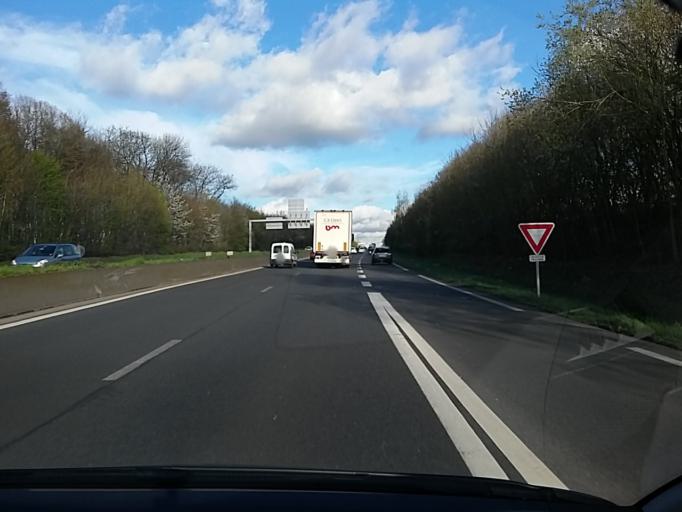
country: FR
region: Picardie
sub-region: Departement de la Somme
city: Poulainville
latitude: 49.9268
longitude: 2.3091
